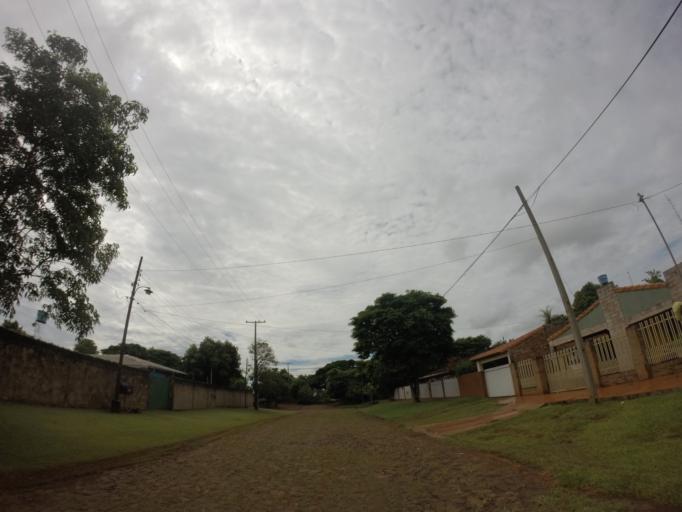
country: PY
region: Alto Parana
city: Ciudad del Este
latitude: -25.4069
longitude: -54.6486
